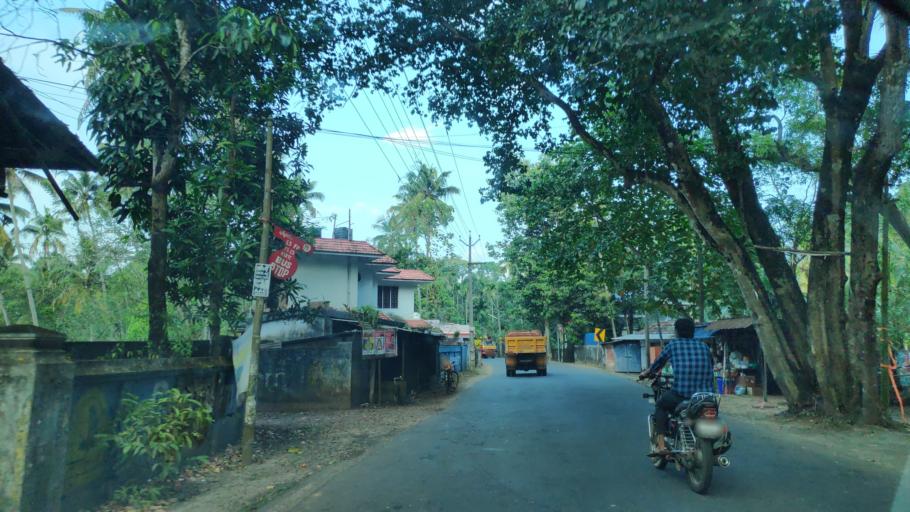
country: IN
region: Kerala
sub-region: Alappuzha
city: Shertallai
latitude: 9.6686
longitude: 76.3882
